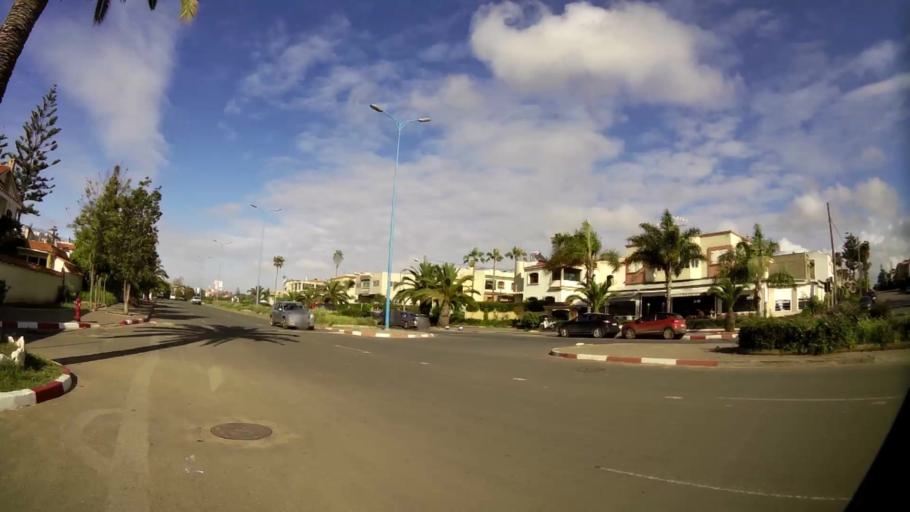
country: MA
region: Grand Casablanca
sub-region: Mohammedia
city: Mohammedia
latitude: 33.7105
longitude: -7.3551
